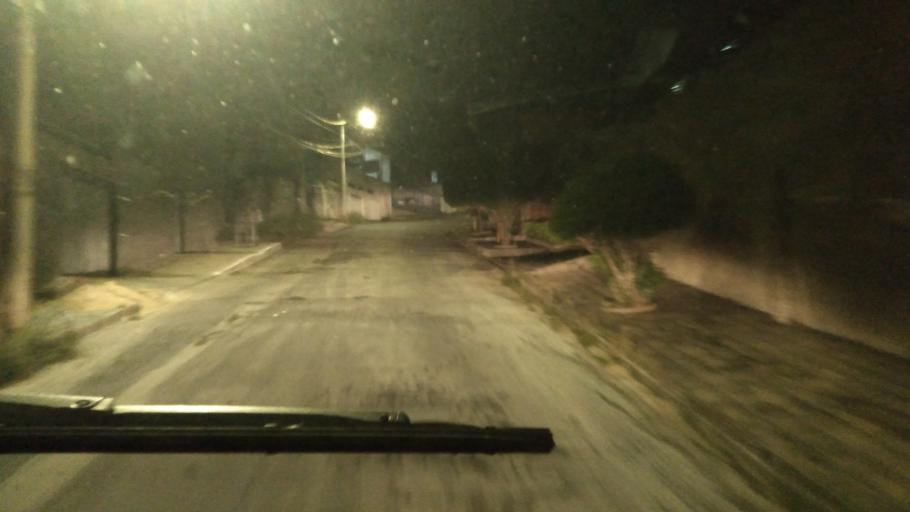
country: BR
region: Minas Gerais
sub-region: Belo Horizonte
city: Belo Horizonte
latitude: -19.8739
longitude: -43.9472
